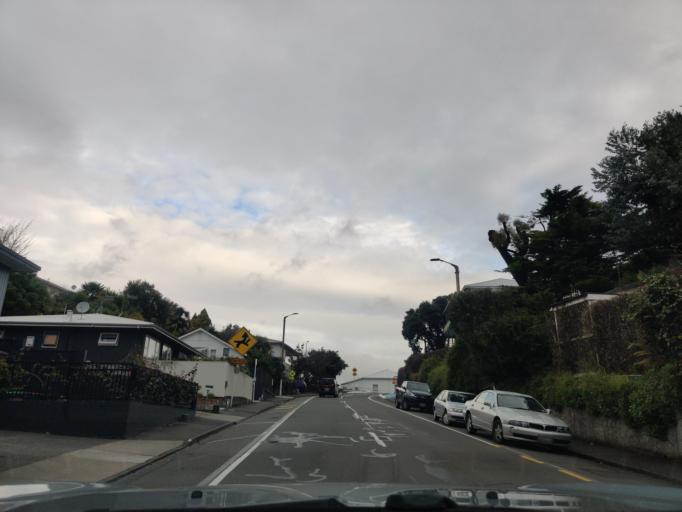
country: NZ
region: Hawke's Bay
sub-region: Napier City
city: Napier
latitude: -39.4851
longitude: 176.9126
